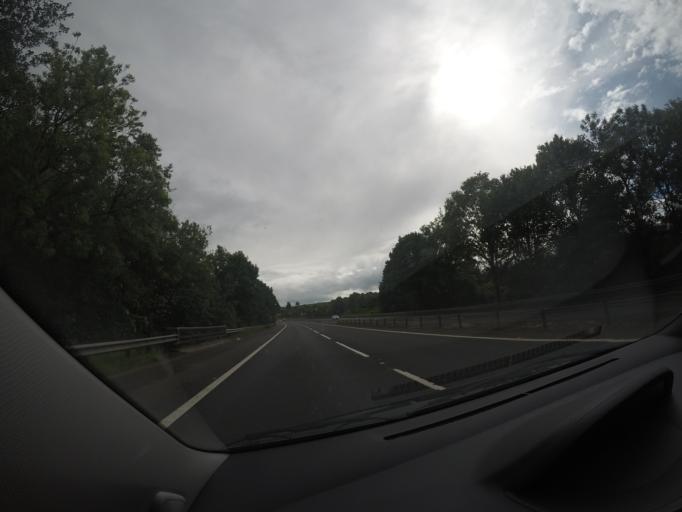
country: GB
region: Scotland
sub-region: Falkirk
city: Dunipace
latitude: 56.0349
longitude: -3.9216
